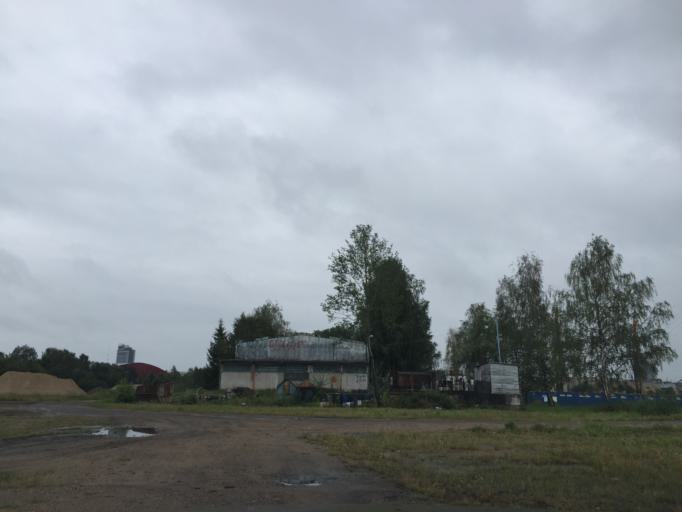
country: LV
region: Riga
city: Riga
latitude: 56.9662
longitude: 24.1116
